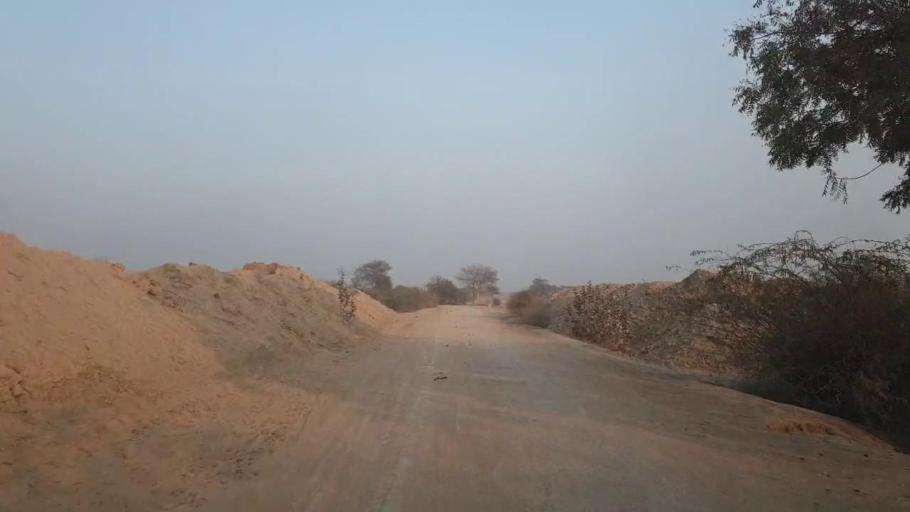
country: PK
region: Sindh
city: Bhit Shah
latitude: 25.7818
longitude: 68.4601
